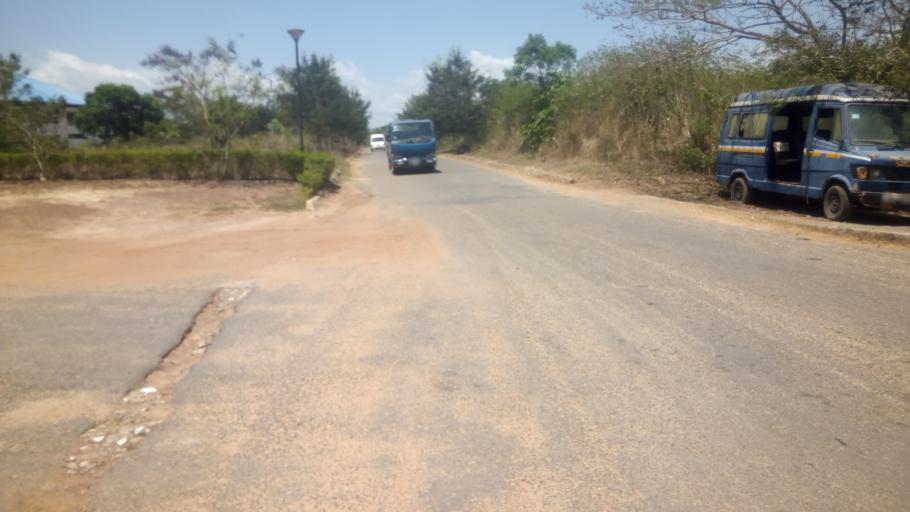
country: GH
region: Central
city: Cape Coast
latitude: 5.1189
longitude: -1.2897
